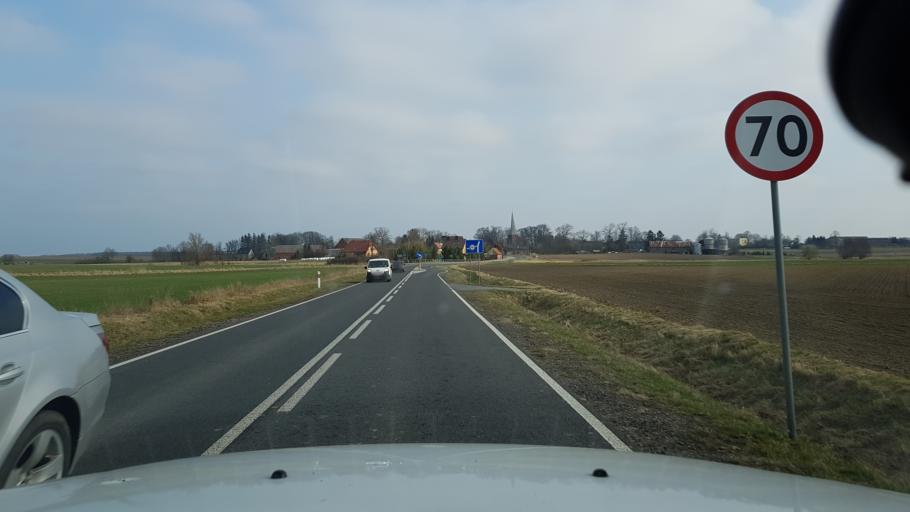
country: PL
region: West Pomeranian Voivodeship
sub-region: Powiat koszalinski
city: Sianow
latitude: 54.2901
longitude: 16.2720
